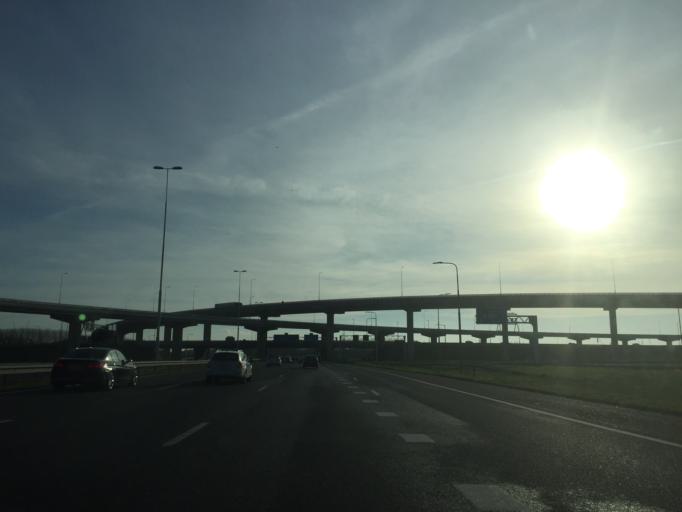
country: NL
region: South Holland
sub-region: Gemeente Ridderkerk
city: Ridderkerk
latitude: 51.8767
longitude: 4.5688
